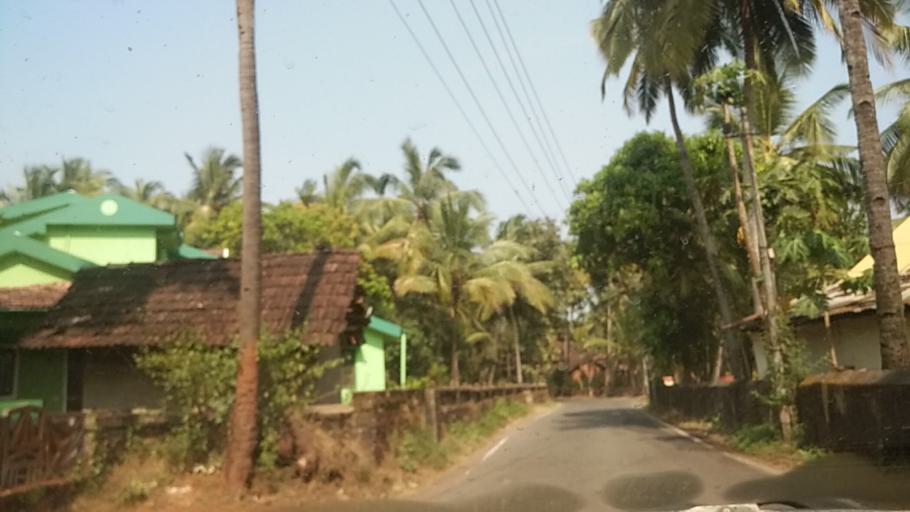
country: IN
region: Goa
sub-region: South Goa
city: Cavelossim
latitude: 15.1539
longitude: 73.9648
